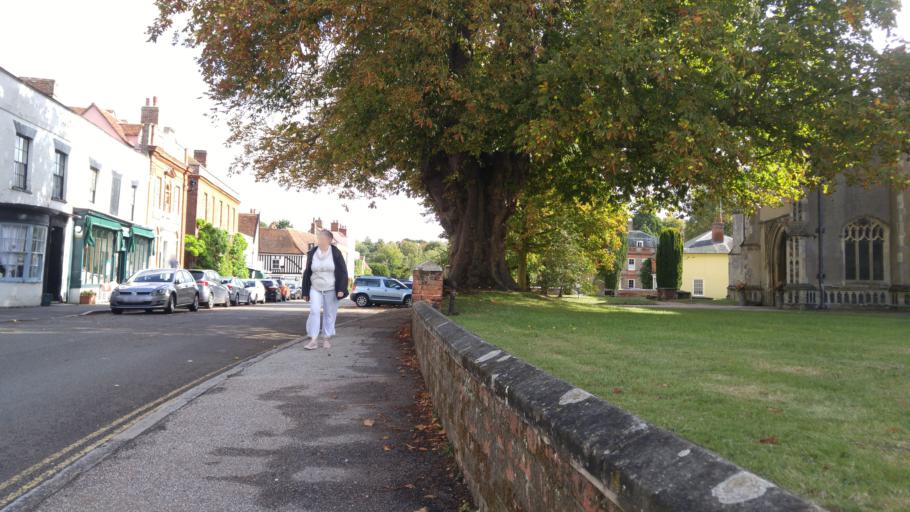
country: GB
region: England
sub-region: Suffolk
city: East Bergholt
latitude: 51.9588
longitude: 0.9924
